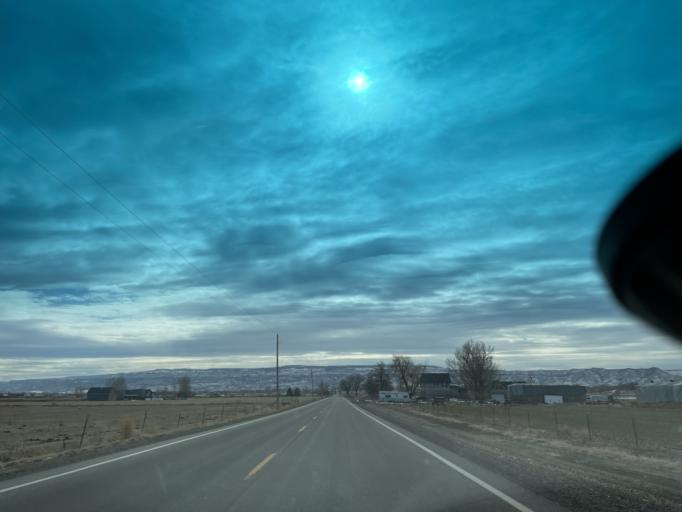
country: US
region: Colorado
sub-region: Mesa County
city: Loma
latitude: 39.2452
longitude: -108.8129
